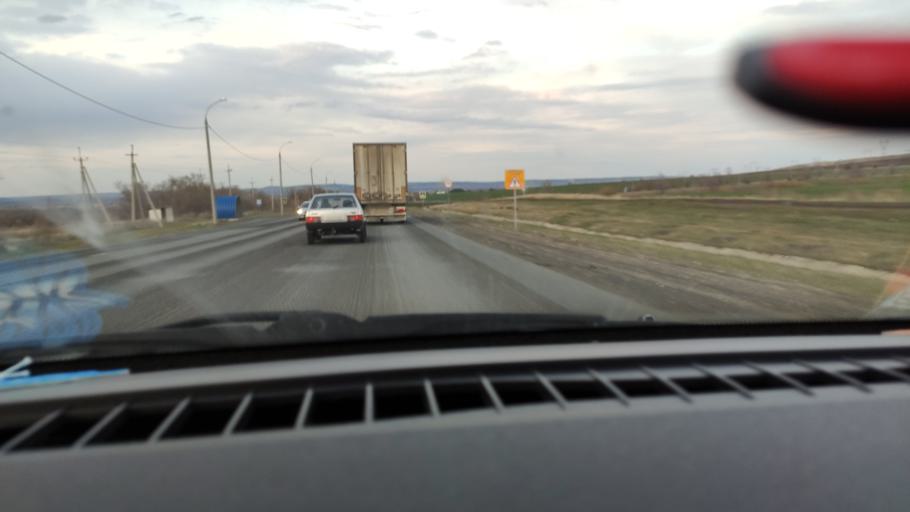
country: RU
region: Saratov
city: Shumeyka
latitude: 51.7905
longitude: 46.1514
